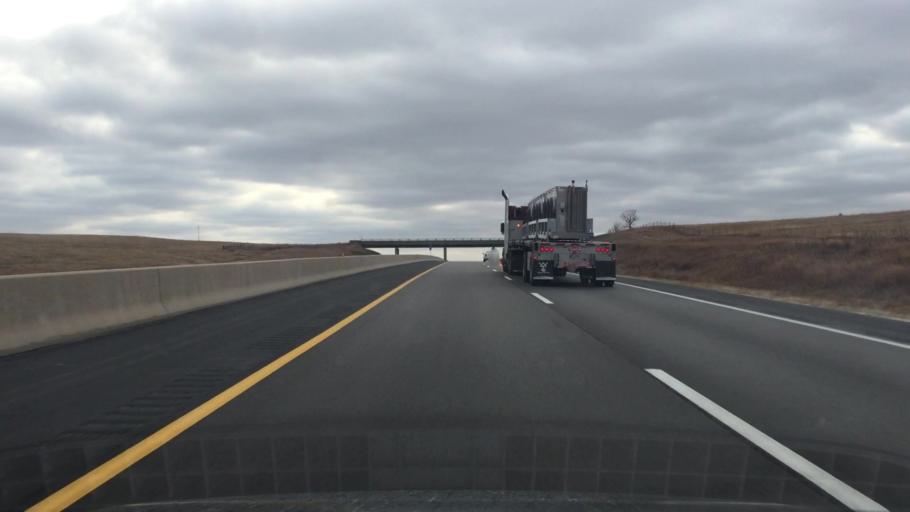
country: US
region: Kansas
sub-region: Chase County
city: Cottonwood Falls
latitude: 38.1635
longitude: -96.4824
